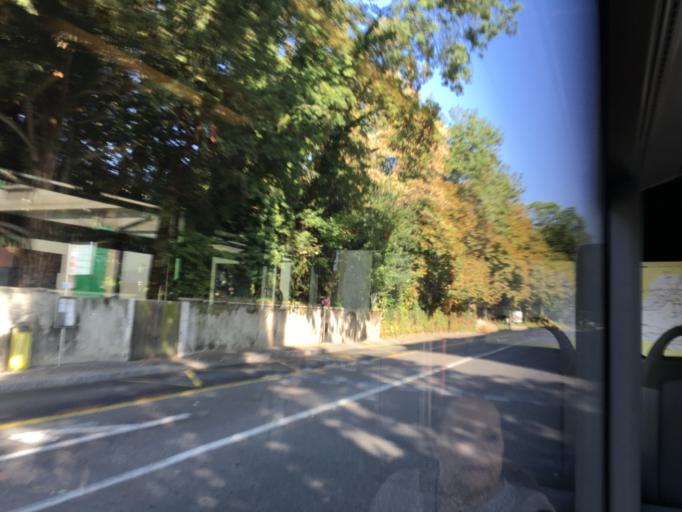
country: CH
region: Geneva
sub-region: Geneva
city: Geneve
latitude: 46.2166
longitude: 6.1413
